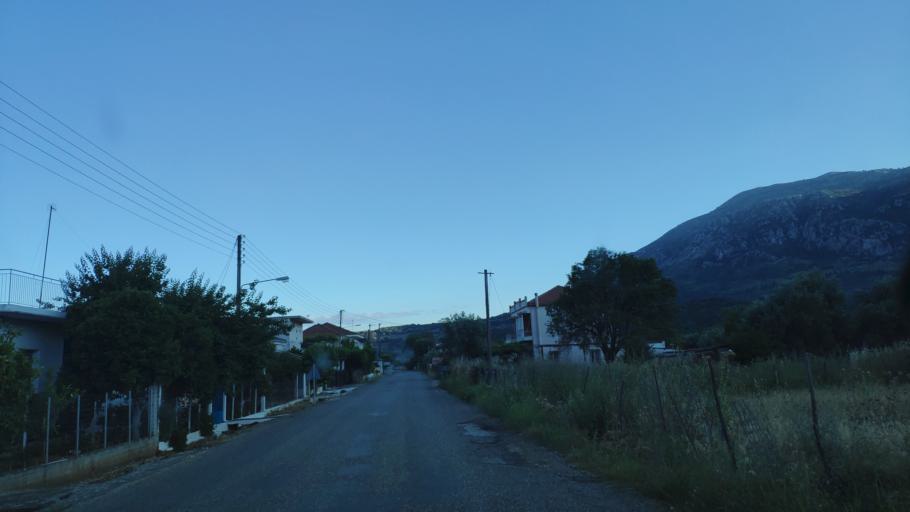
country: GR
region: West Greece
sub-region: Nomos Aitolias kai Akarnanias
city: Astakos
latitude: 38.5847
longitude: 21.0896
